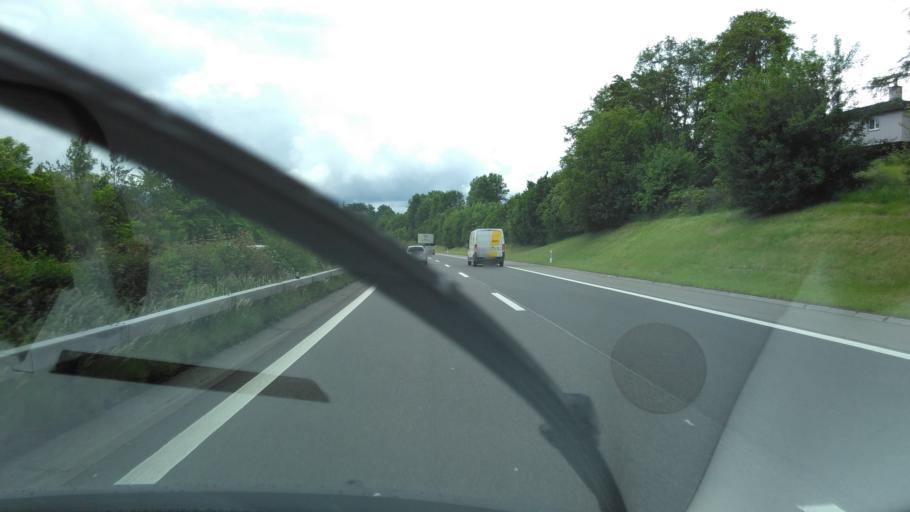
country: CH
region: Zurich
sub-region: Bezirk Horgen
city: Adliswil / Tal
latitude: 47.3112
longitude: 8.5423
